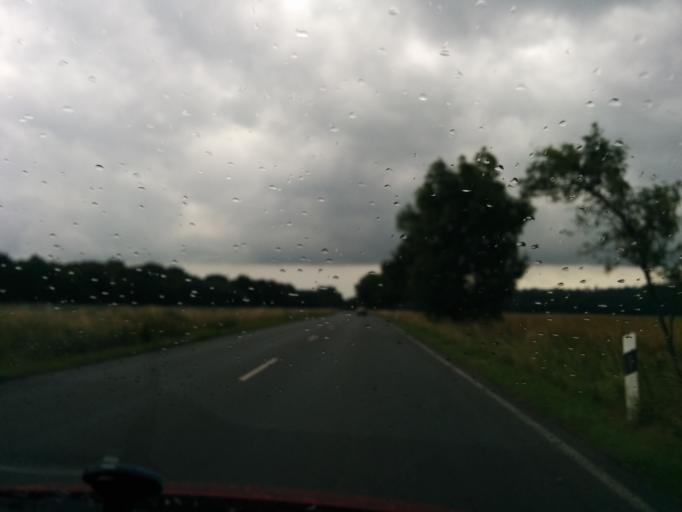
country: DE
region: Lower Saxony
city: Bad Sachsa
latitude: 51.5749
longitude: 10.5165
